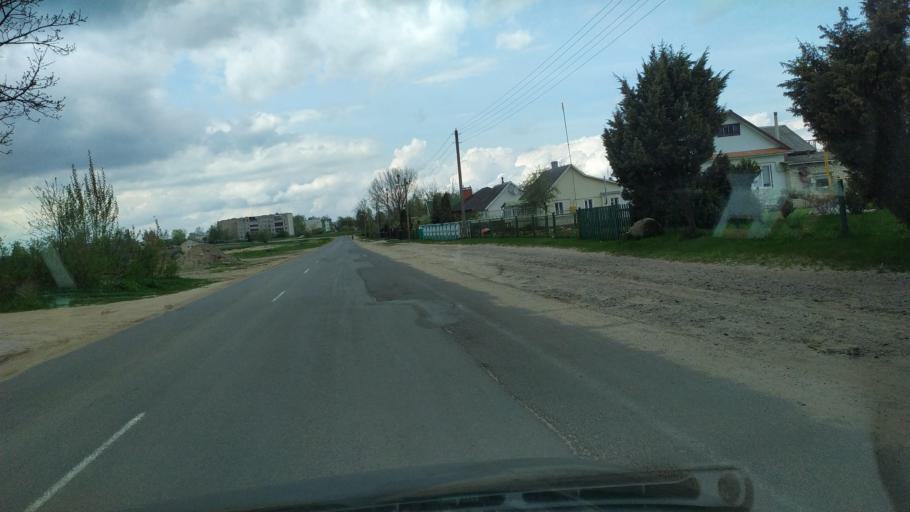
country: BY
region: Brest
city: Pruzhany
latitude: 52.5615
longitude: 24.4252
